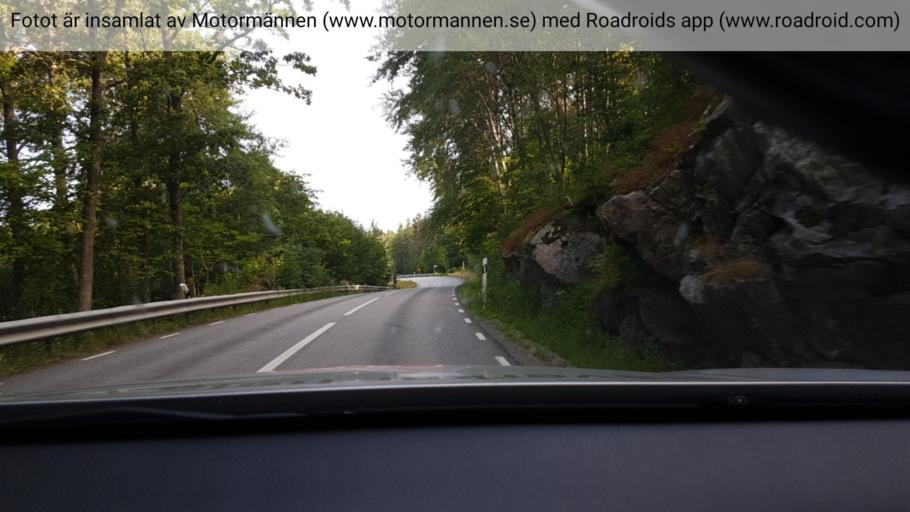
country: SE
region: Stockholm
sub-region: Norrtalje Kommun
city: Rimbo
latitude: 59.6935
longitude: 18.3687
